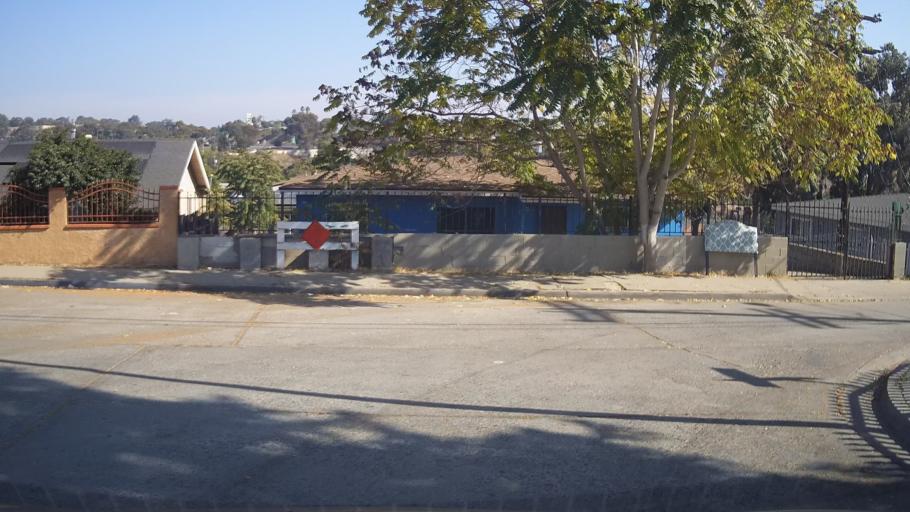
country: US
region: California
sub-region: San Diego County
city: San Diego
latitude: 32.7106
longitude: -117.1242
